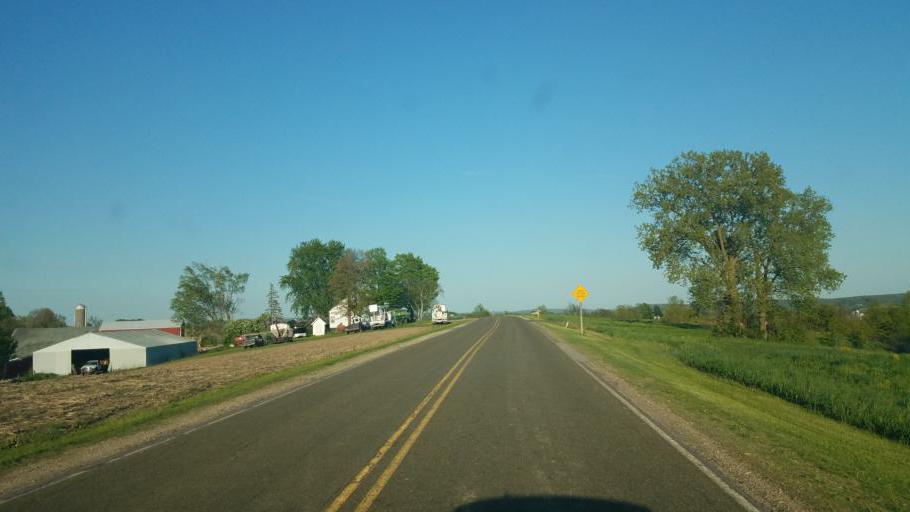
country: US
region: Wisconsin
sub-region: Vernon County
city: Hillsboro
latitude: 43.6437
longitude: -90.2752
